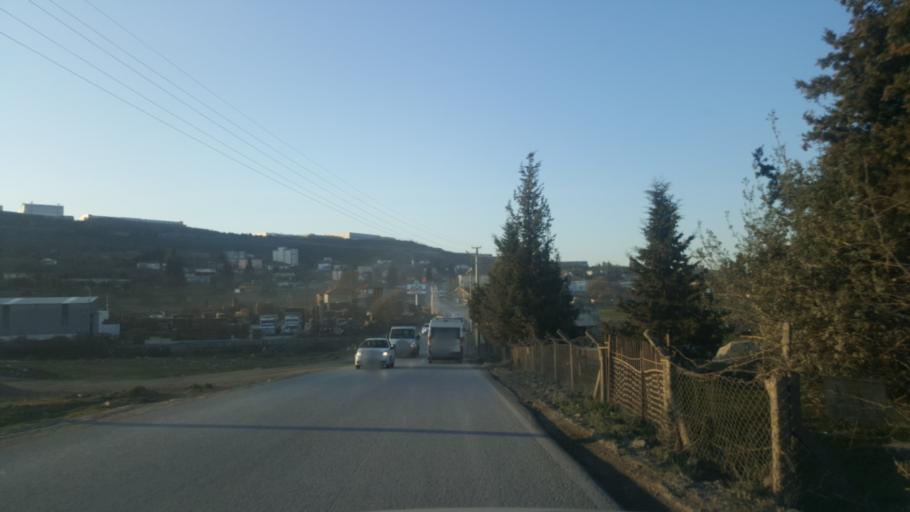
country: TR
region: Kocaeli
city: Tavsanli
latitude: 40.8512
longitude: 29.5552
